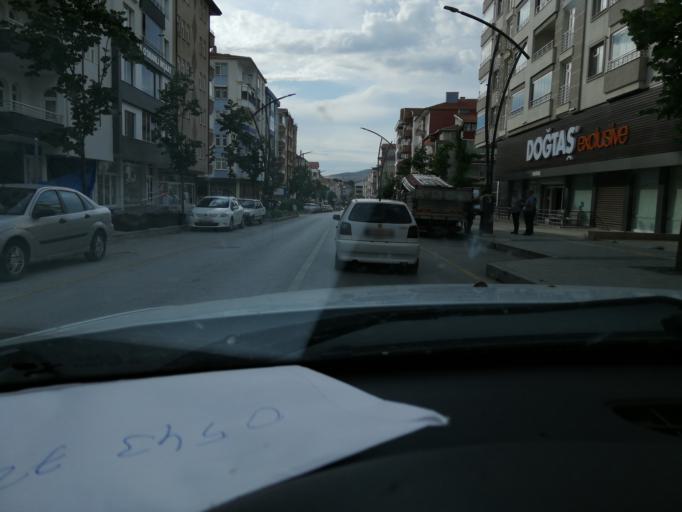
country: TR
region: Kirsehir
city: Kirsehir
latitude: 39.1402
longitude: 34.1645
